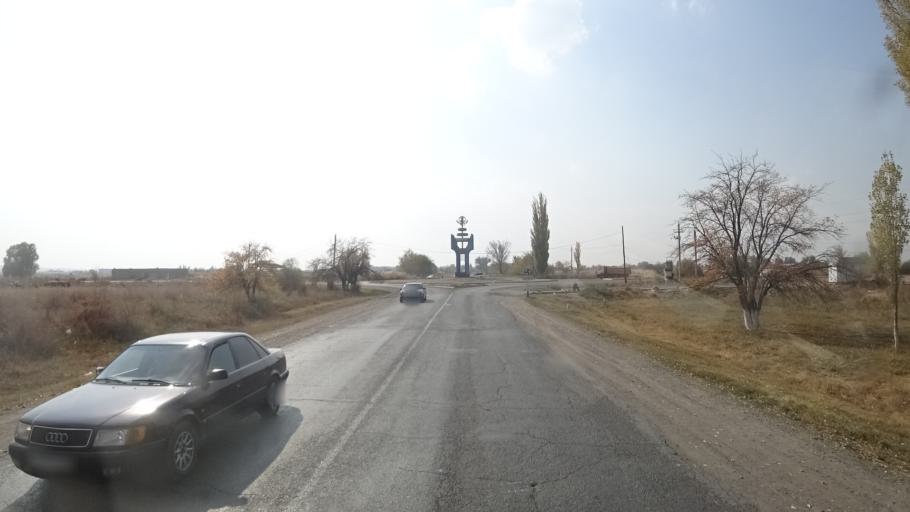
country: KZ
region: Zhambyl
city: Sarykemer
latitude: 42.9381
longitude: 71.4443
